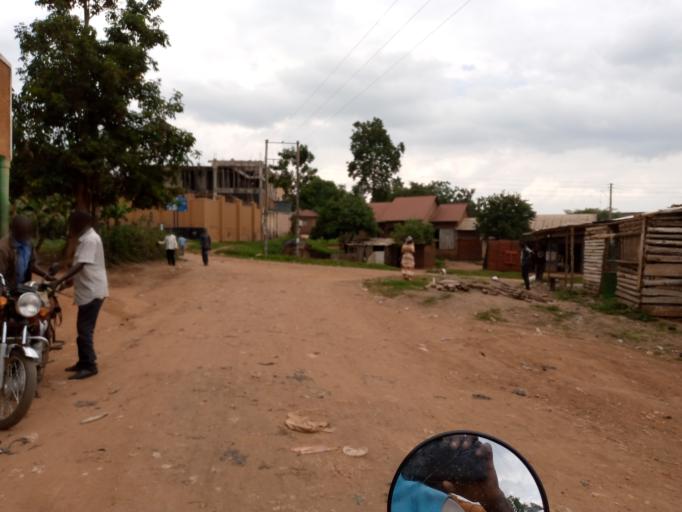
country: UG
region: Eastern Region
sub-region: Mbale District
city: Mbale
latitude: 1.0846
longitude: 34.1673
